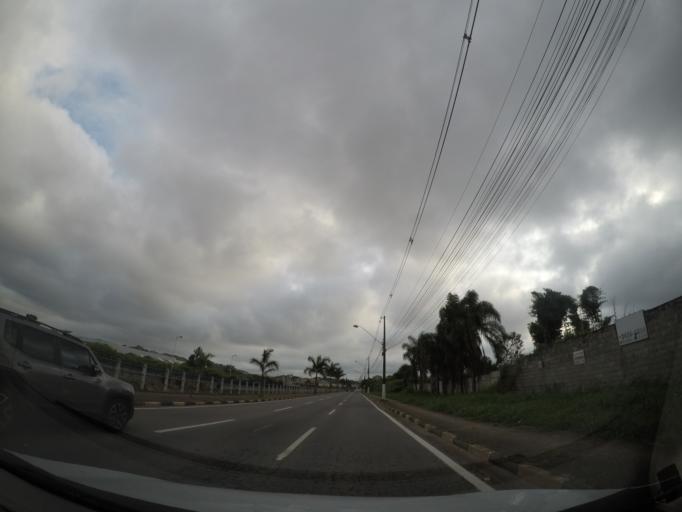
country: BR
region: Sao Paulo
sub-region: Aruja
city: Aruja
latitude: -23.4054
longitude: -46.3650
